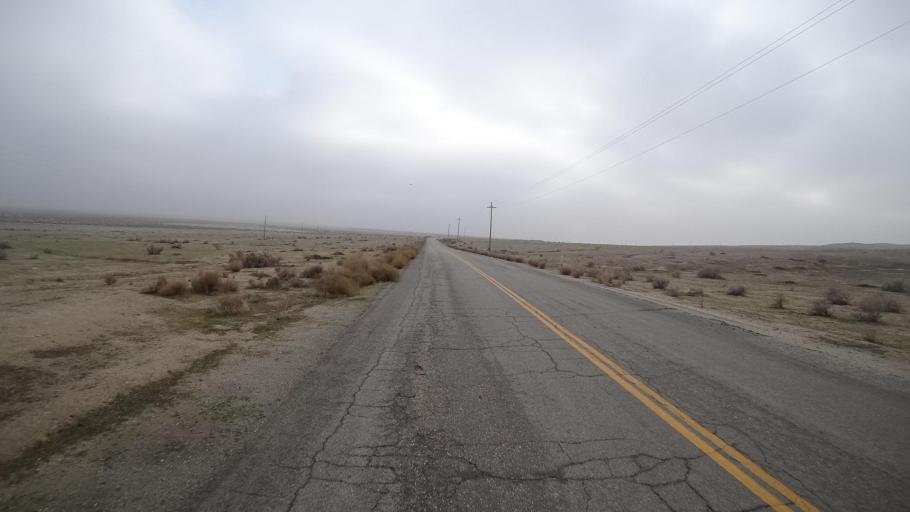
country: US
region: California
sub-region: Kern County
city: Maricopa
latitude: 35.1424
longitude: -119.3417
